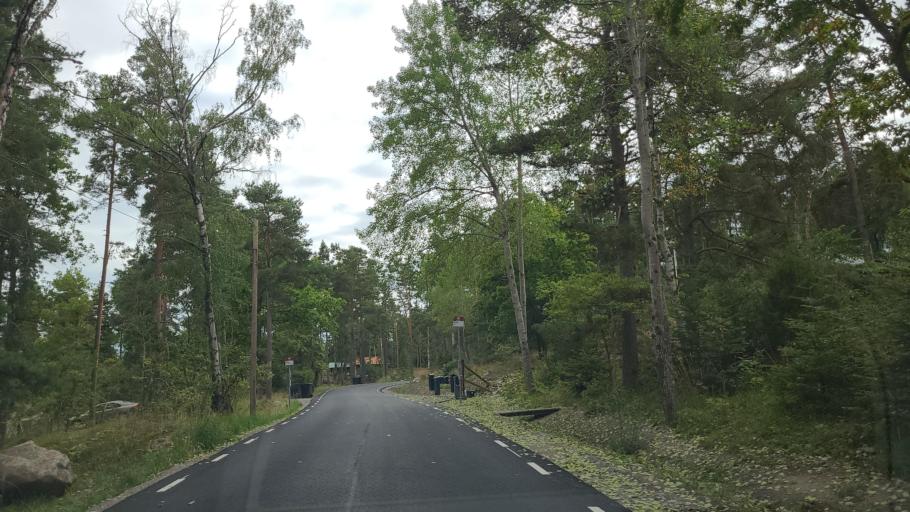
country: SE
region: Stockholm
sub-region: Upplands-Bro Kommun
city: Bro
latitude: 59.4837
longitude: 17.6004
